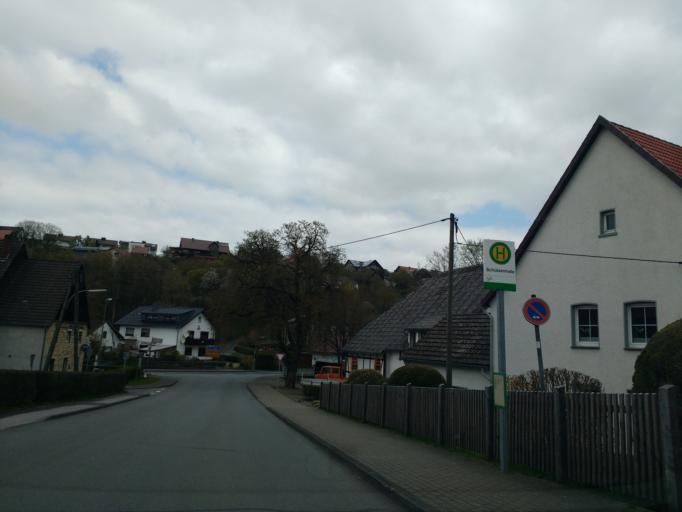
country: DE
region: North Rhine-Westphalia
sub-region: Regierungsbezirk Detmold
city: Wunnenberg
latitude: 51.5096
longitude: 8.7429
